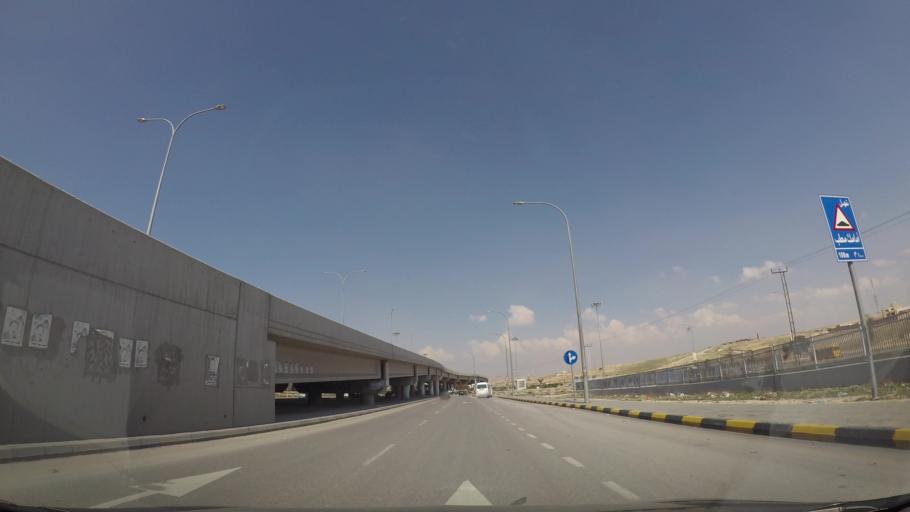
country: JO
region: Zarqa
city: Zarqa
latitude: 32.0797
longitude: 36.1060
